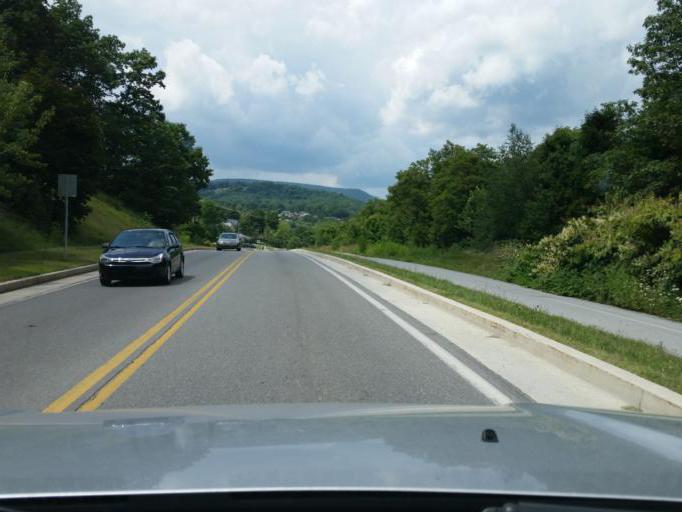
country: US
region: Pennsylvania
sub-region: Blair County
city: Altoona
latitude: 40.5332
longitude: -78.3941
